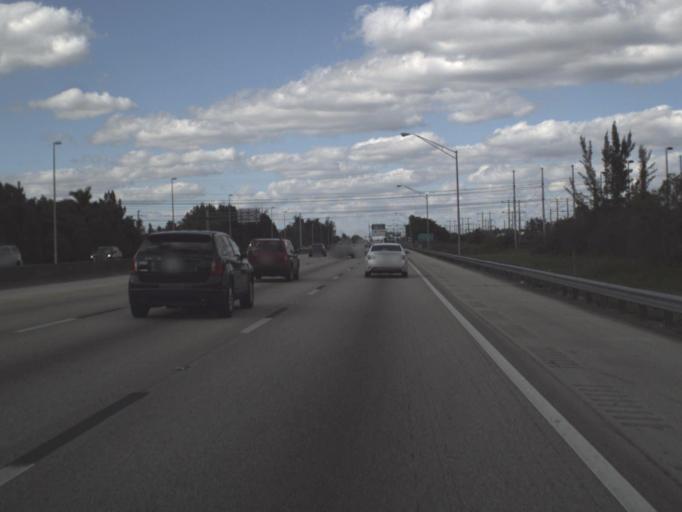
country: US
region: Florida
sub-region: Broward County
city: Davie
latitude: 26.0535
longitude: -80.2148
